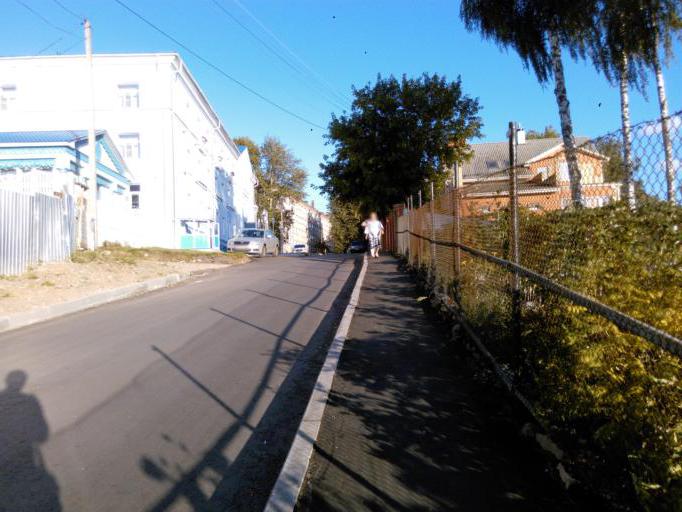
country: RU
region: Kostroma
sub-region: Kostromskoy Rayon
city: Kostroma
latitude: 57.7552
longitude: 40.9502
